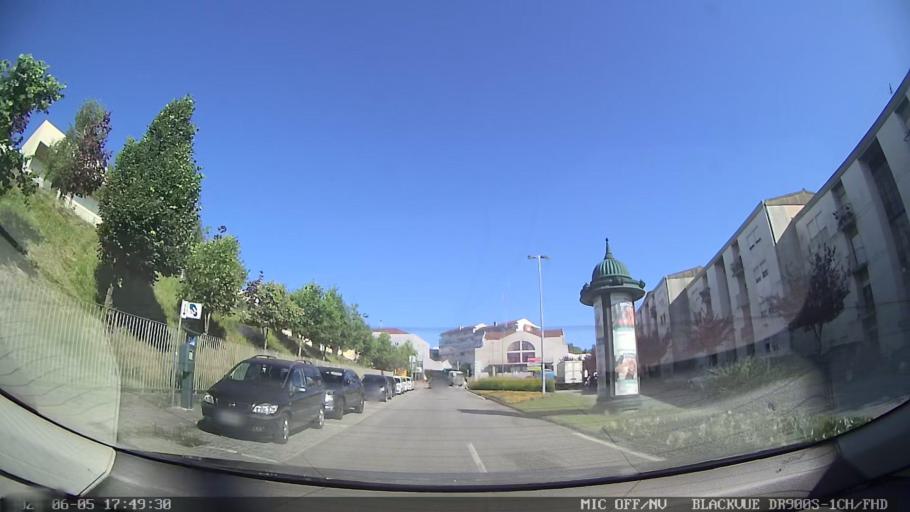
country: PT
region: Porto
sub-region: Penafiel
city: Penafiel
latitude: 41.2086
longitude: -8.2824
